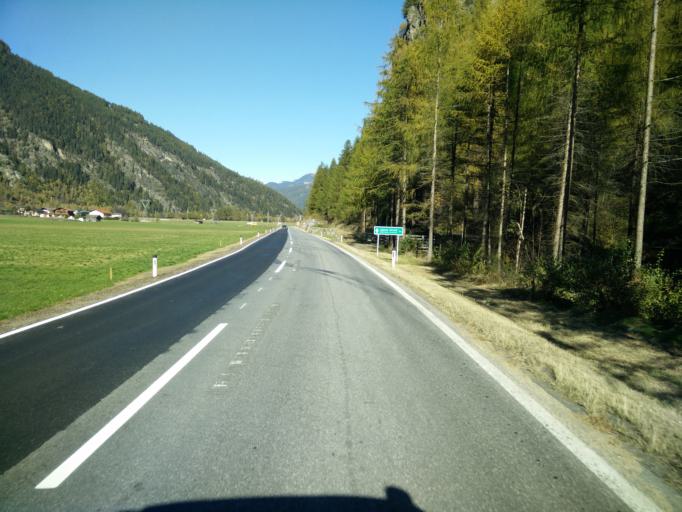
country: AT
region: Tyrol
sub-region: Politischer Bezirk Imst
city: Umhausen
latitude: 47.0538
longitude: 10.9663
